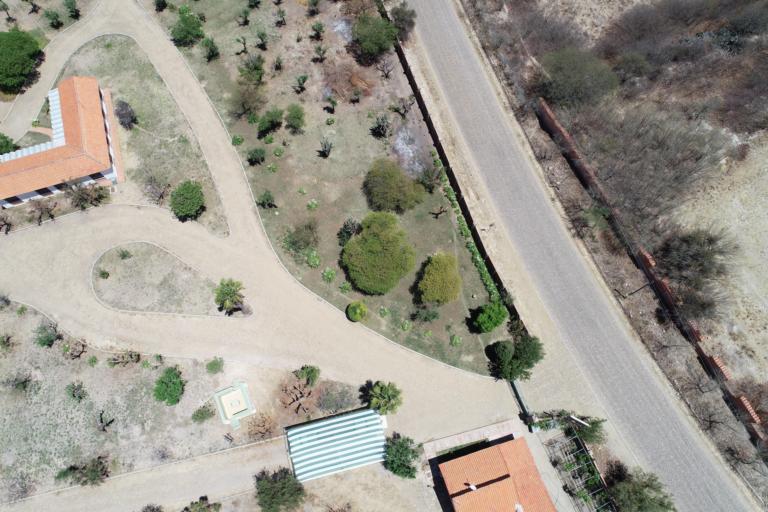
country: BO
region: Tarija
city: Tarija
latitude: -21.5957
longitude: -64.6228
